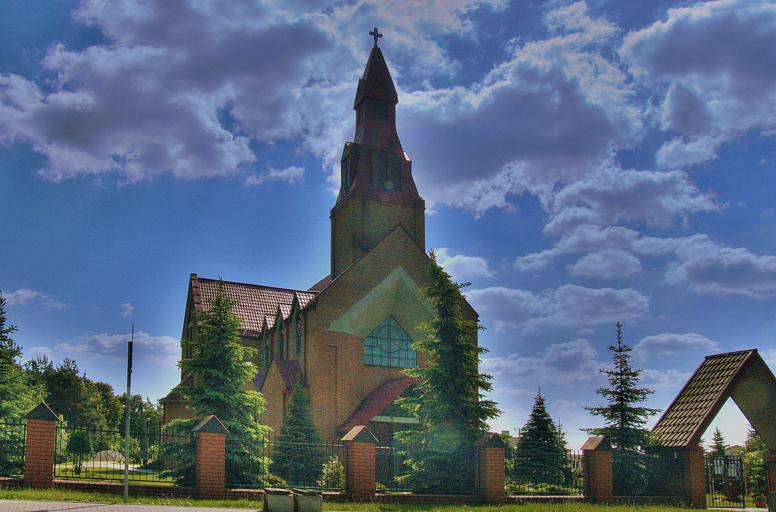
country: PL
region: Lublin Voivodeship
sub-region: Powiat lubartowski
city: Lubartow
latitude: 51.4806
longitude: 22.6003
